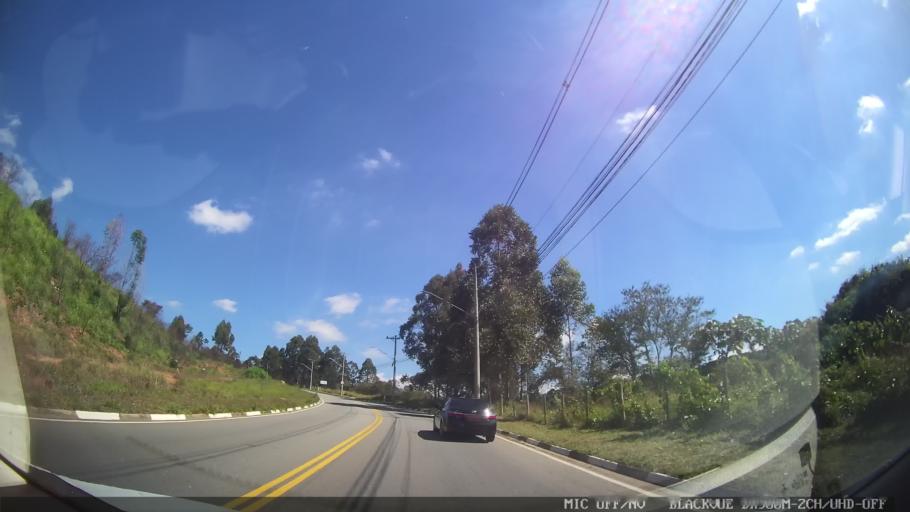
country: BR
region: Sao Paulo
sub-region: Barueri
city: Barueri
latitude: -23.4449
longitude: -46.8358
